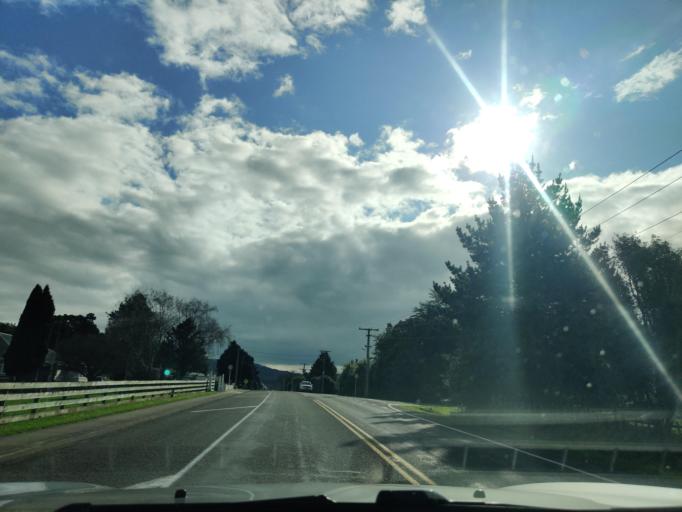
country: NZ
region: Manawatu-Wanganui
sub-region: Palmerston North City
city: Palmerston North
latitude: -40.3395
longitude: 175.8763
